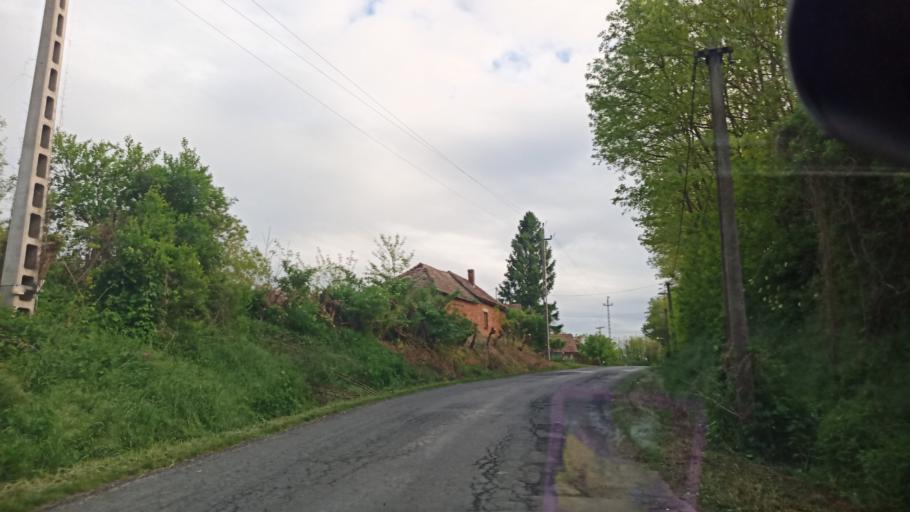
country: HU
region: Zala
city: Pacsa
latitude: 46.7291
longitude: 17.0036
